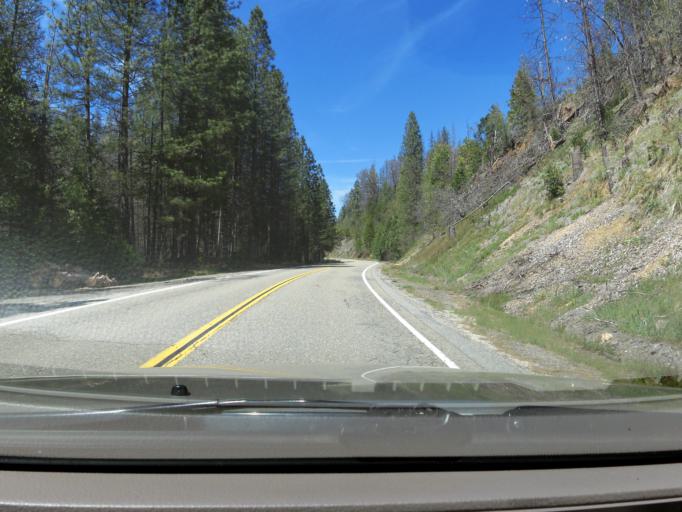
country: US
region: California
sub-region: Madera County
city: Oakhurst
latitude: 37.2800
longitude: -119.5762
